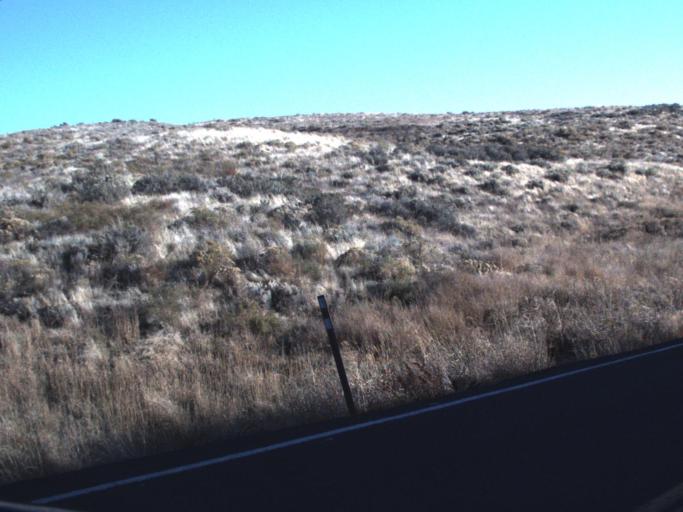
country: US
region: Washington
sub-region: Adams County
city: Ritzville
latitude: 46.6954
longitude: -118.3902
